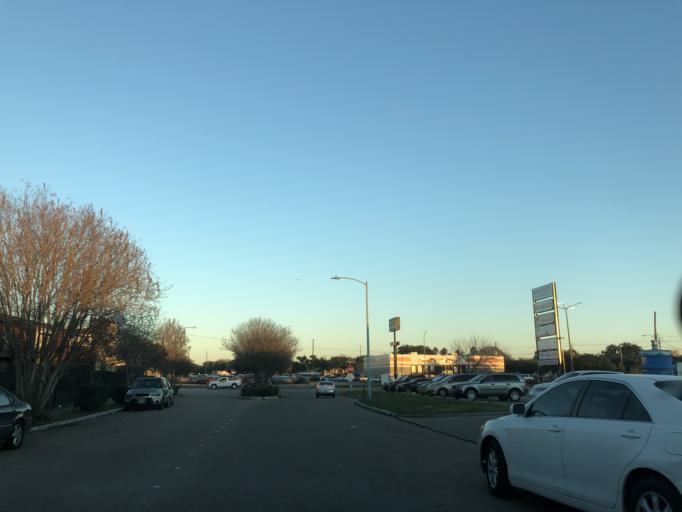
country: US
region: Texas
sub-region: Harris County
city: Bellaire
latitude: 29.6879
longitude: -95.5098
